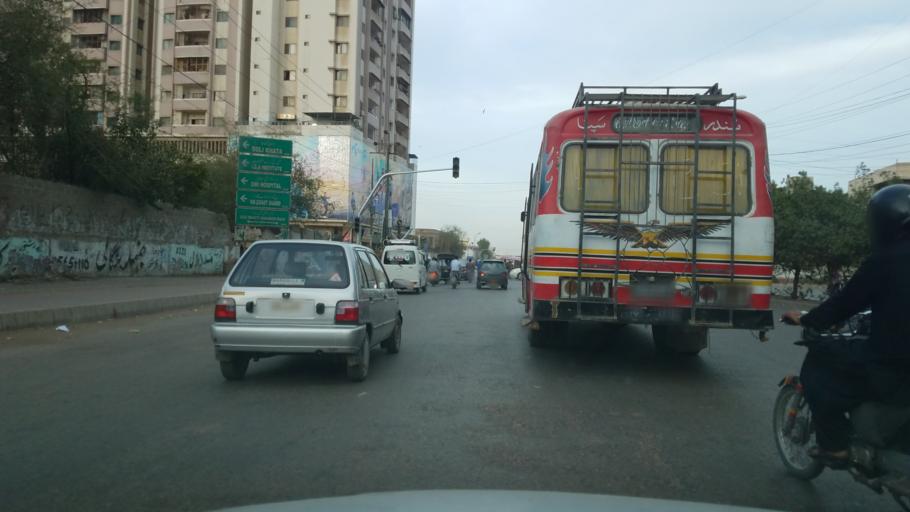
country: PK
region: Sindh
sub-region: Karachi District
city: Karachi
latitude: 24.8659
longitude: 67.0259
